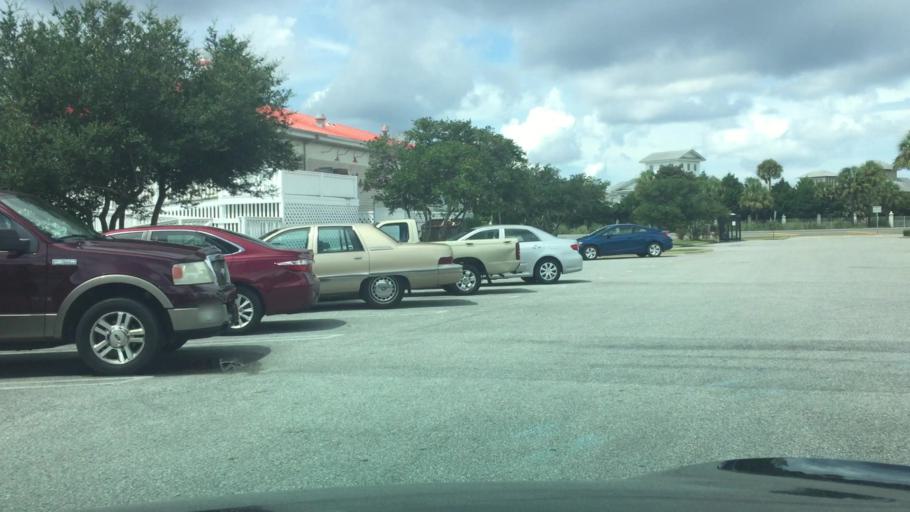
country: US
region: Florida
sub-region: Bay County
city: Laguna Beach
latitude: 30.2628
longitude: -85.9738
